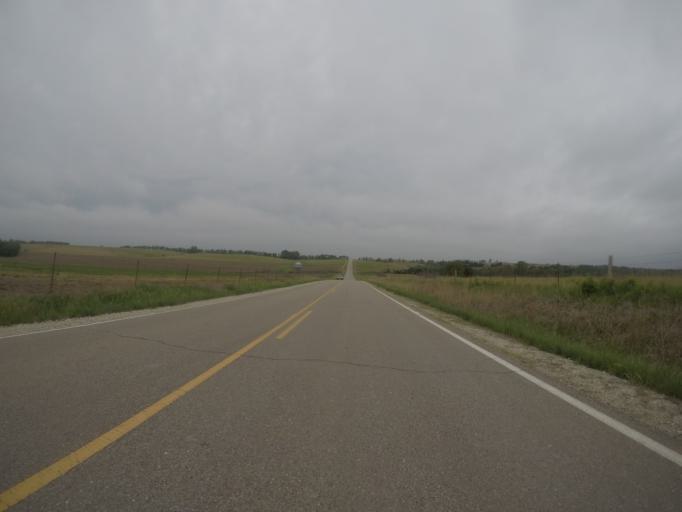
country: US
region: Kansas
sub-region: Pottawatomie County
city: Westmoreland
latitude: 39.5217
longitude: -96.2396
